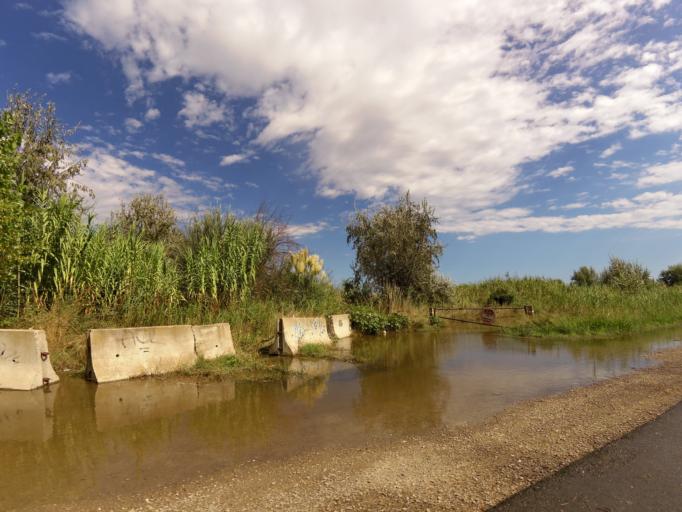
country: FR
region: Languedoc-Roussillon
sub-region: Departement du Gard
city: Le Grau-du-Roi
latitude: 43.5219
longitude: 4.1498
